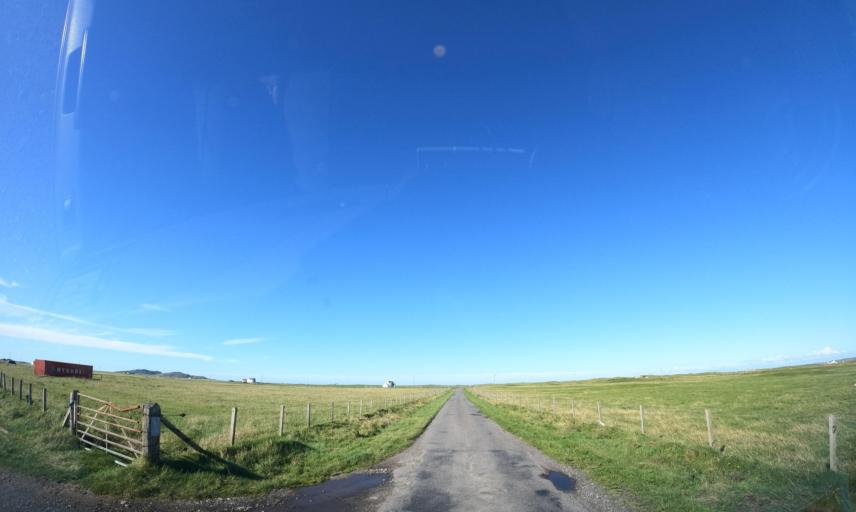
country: GB
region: Scotland
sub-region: Eilean Siar
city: Barra
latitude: 56.4749
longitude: -6.8994
